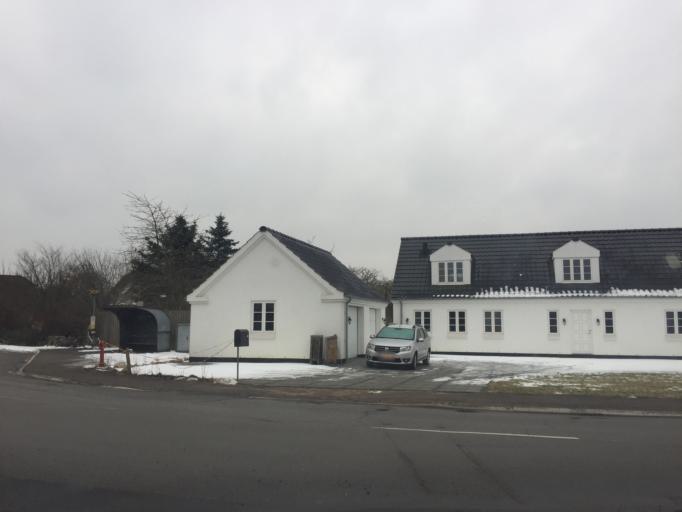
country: DK
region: Capital Region
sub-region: Hoje-Taastrup Kommune
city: Taastrup
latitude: 55.6857
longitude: 12.2922
